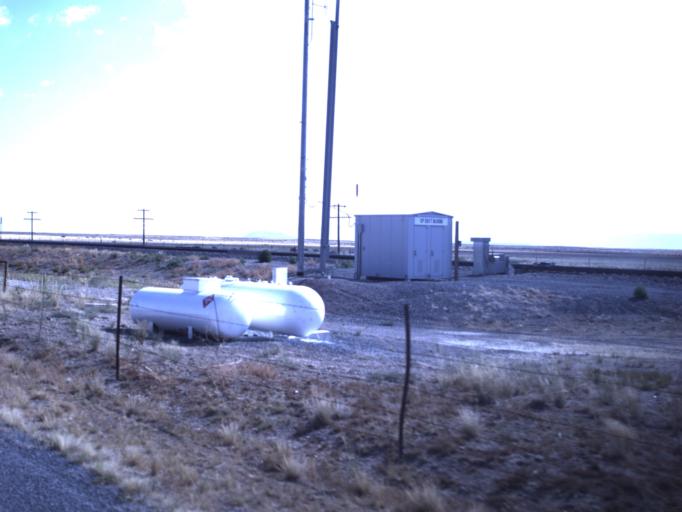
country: US
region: Utah
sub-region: Millard County
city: Fillmore
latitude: 38.9204
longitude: -112.8119
